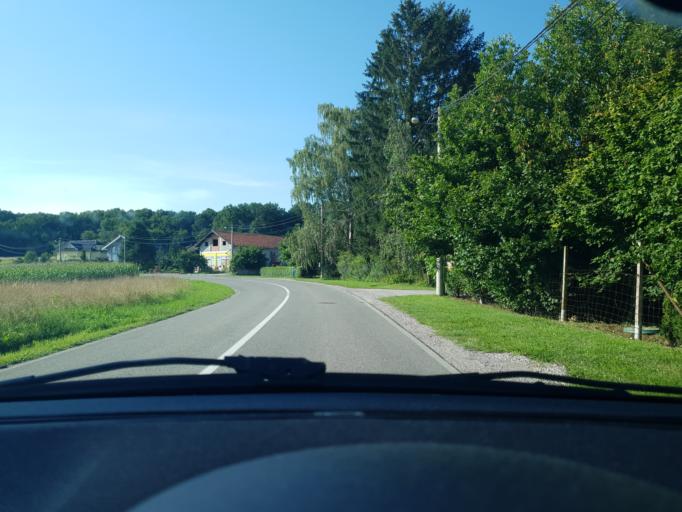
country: HR
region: Zagrebacka
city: Jablanovec
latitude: 45.9105
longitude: 15.8530
